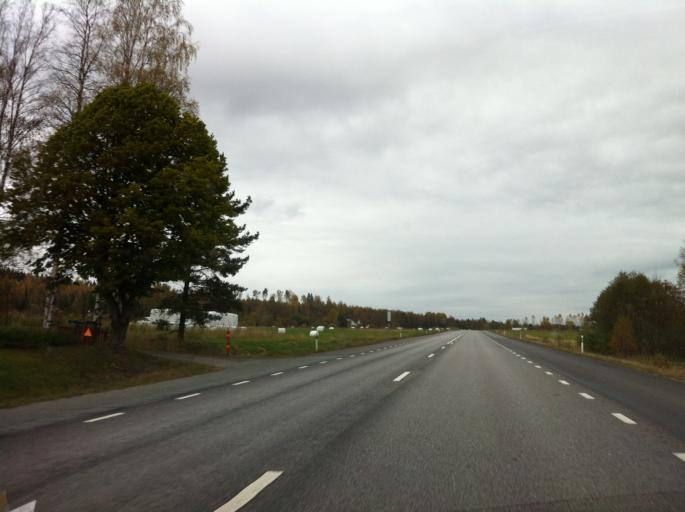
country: SE
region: OErebro
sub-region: Lindesbergs Kommun
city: Stora
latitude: 59.7266
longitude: 15.1343
